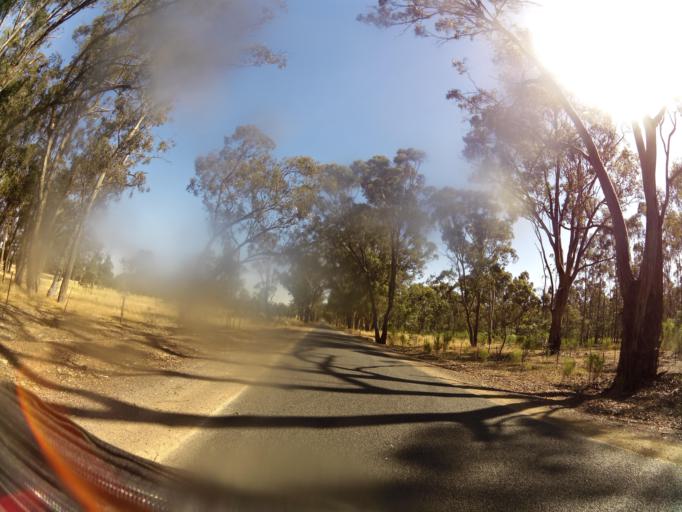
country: AU
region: Victoria
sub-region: Campaspe
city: Kyabram
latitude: -36.8690
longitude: 145.0868
